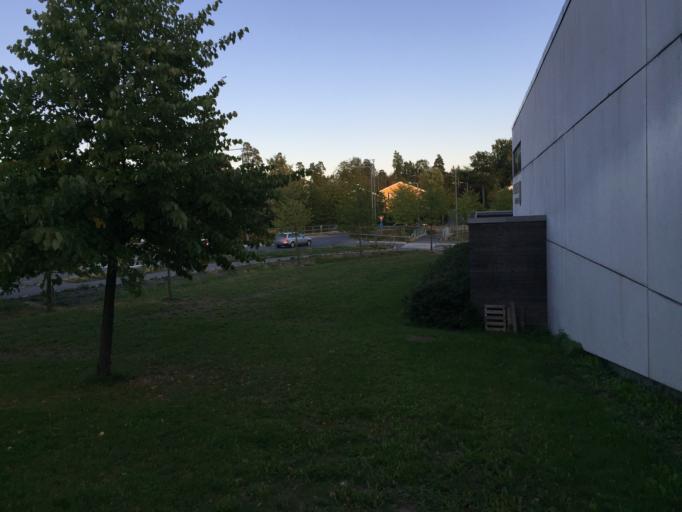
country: NO
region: Akershus
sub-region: Baerum
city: Lysaker
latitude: 59.8905
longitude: 10.6211
